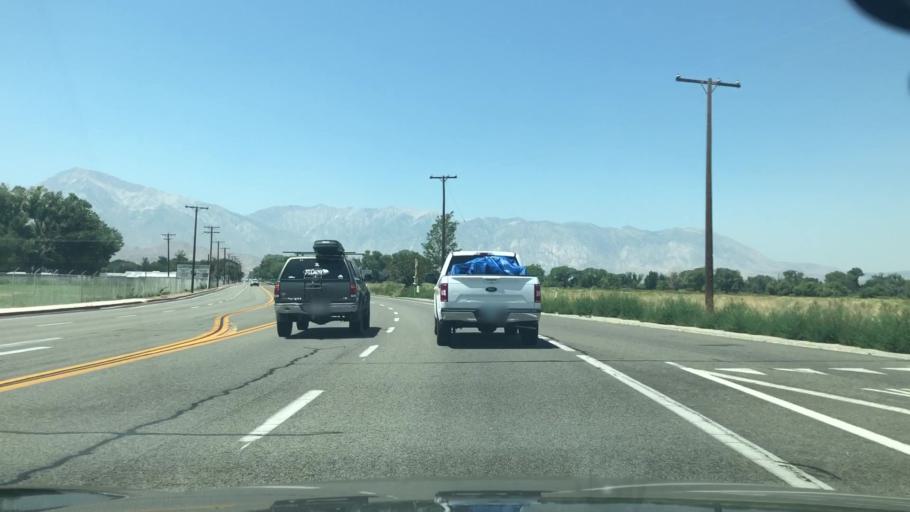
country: US
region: California
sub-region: Inyo County
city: Bishop
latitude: 37.3739
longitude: -118.3980
